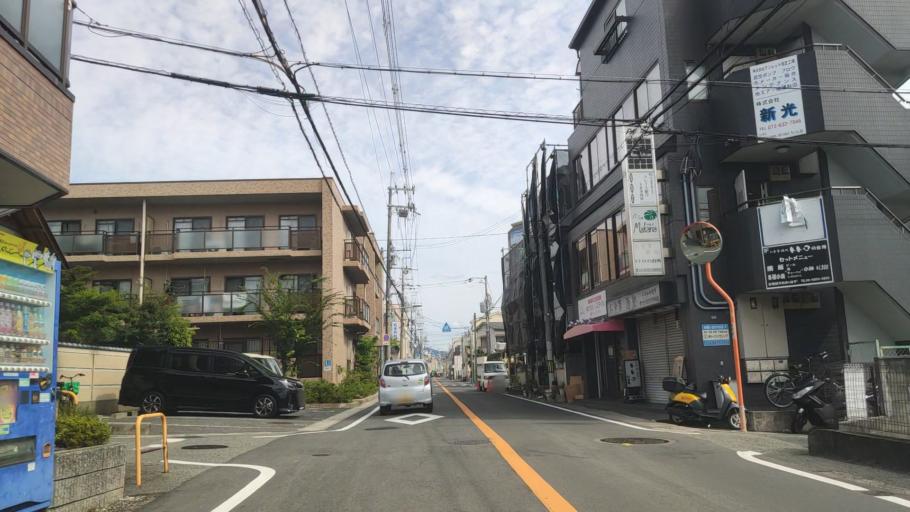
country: JP
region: Osaka
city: Mino
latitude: 34.8092
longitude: 135.4657
